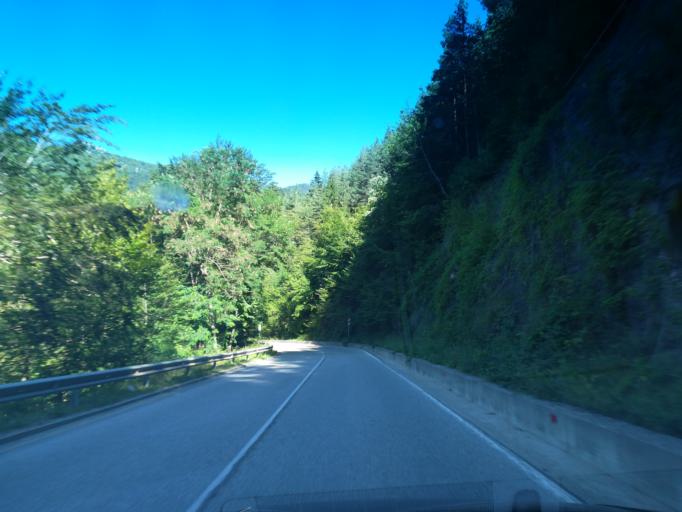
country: BG
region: Smolyan
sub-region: Obshtina Chepelare
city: Chepelare
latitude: 41.8180
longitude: 24.6972
